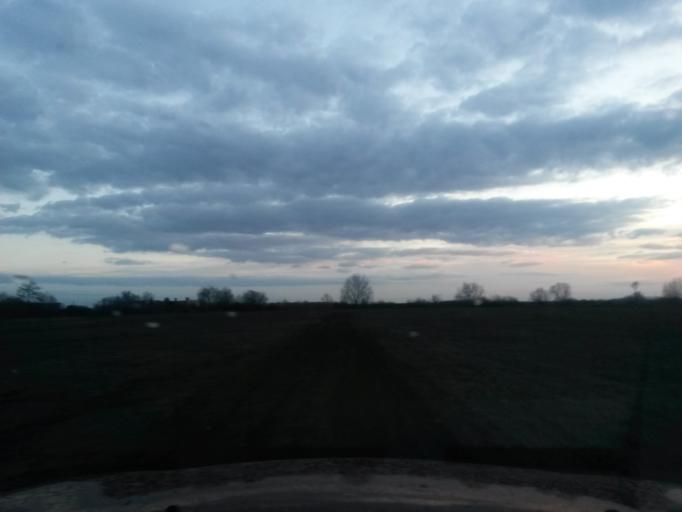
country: SK
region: Kosicky
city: Sobrance
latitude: 48.6916
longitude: 22.0529
